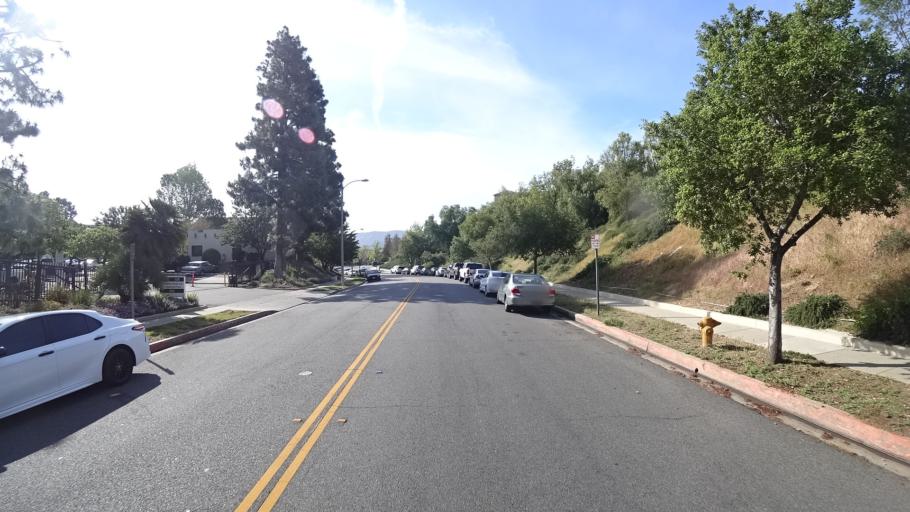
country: US
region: California
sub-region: Ventura County
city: Thousand Oaks
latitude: 34.1862
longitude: -118.8784
